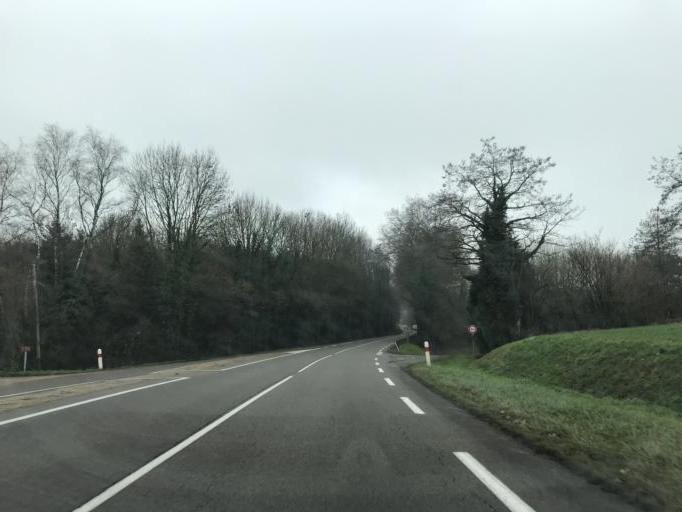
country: FR
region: Rhone-Alpes
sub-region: Departement de l'Ain
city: Peronnas
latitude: 46.1616
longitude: 5.1895
